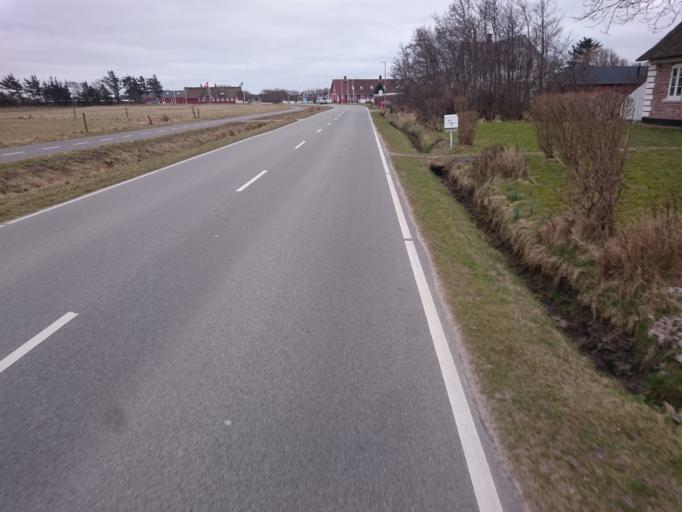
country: DK
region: South Denmark
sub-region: Fano Kommune
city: Nordby
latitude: 55.4281
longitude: 8.3917
